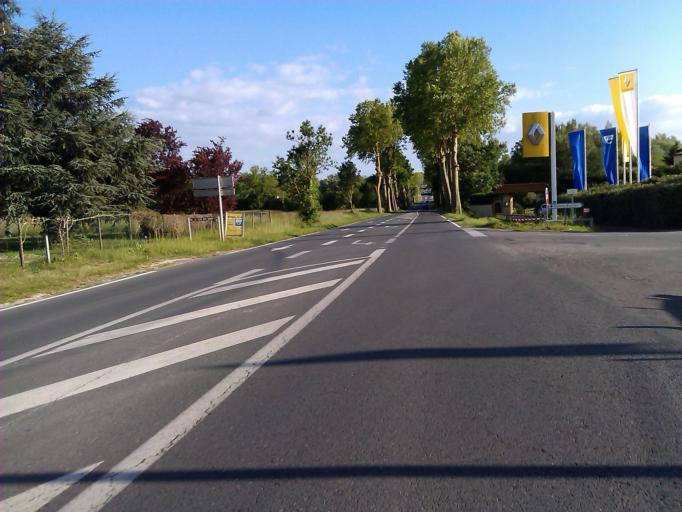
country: FR
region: Aquitaine
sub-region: Departement de la Gironde
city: Cubzac-les-Ponts
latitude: 44.9849
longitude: -0.4508
